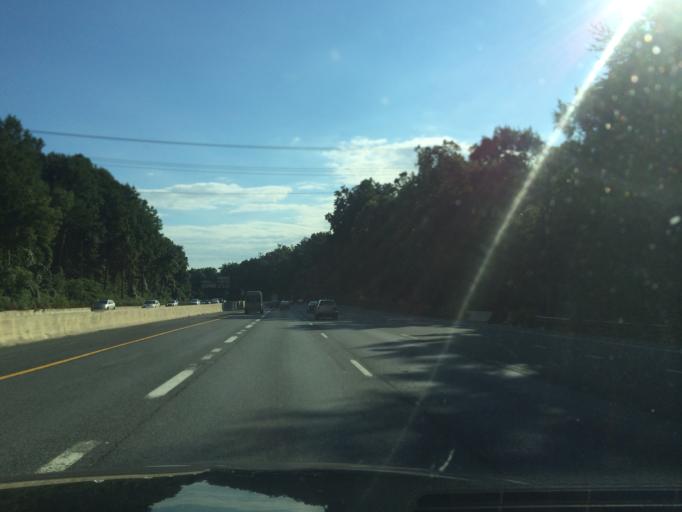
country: US
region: Maryland
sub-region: Montgomery County
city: North Bethesda
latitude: 39.0188
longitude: -77.1457
